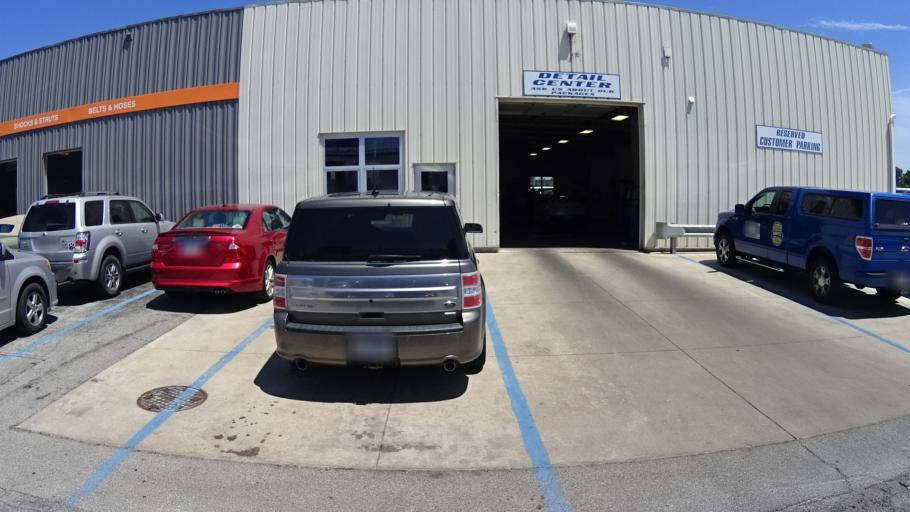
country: US
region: Ohio
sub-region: Erie County
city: Sandusky
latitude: 41.4322
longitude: -82.6900
